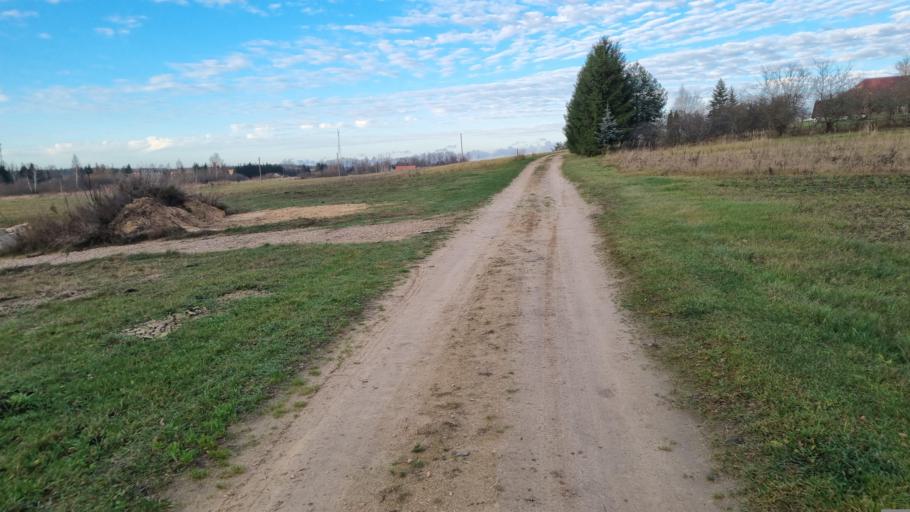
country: LV
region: Kekava
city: Kekava
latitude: 56.7857
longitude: 24.2481
